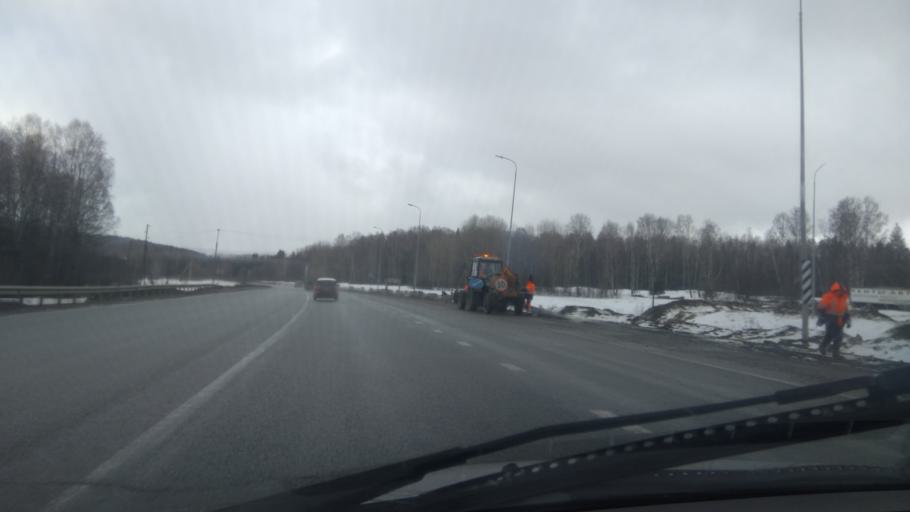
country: RU
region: Sverdlovsk
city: Ufimskiy
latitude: 56.7815
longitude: 58.4029
